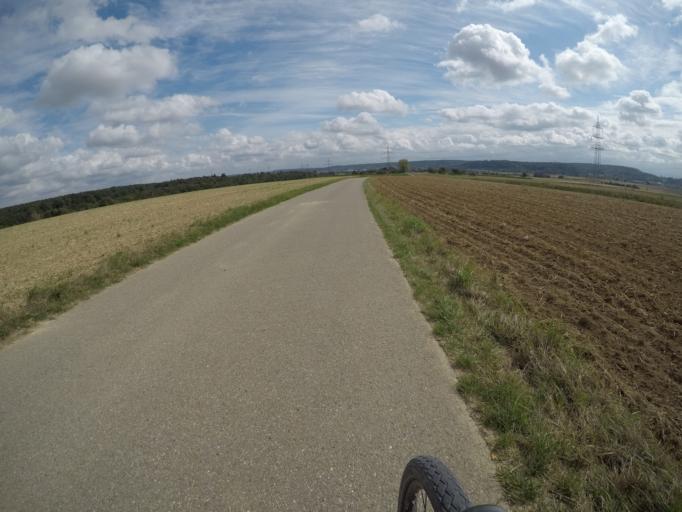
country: DE
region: Baden-Wuerttemberg
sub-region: Regierungsbezirk Stuttgart
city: Herrenberg
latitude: 48.6251
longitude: 8.8553
